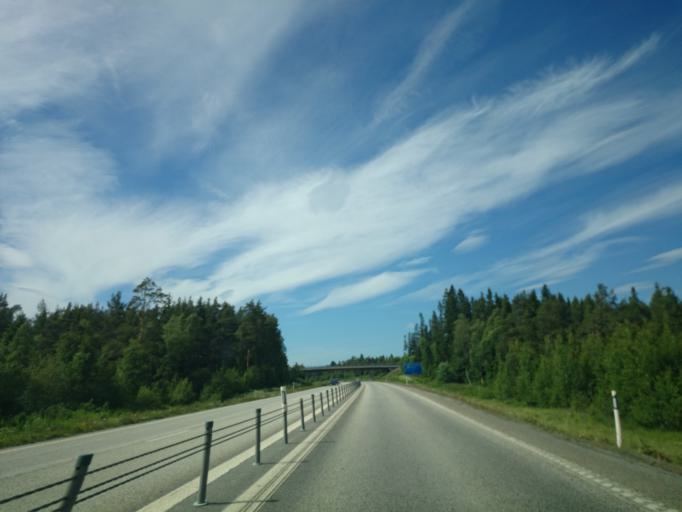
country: SE
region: Jaemtland
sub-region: OEstersunds Kommun
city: Ostersund
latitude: 63.2102
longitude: 14.6638
